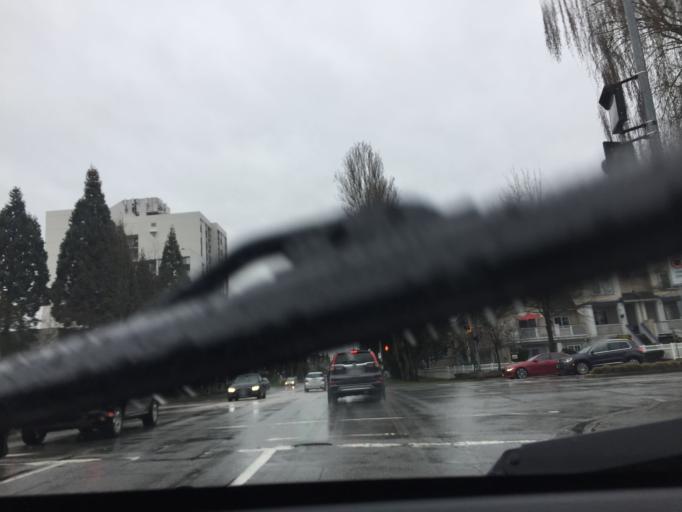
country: CA
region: British Columbia
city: Richmond
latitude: 49.1631
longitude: -123.1479
